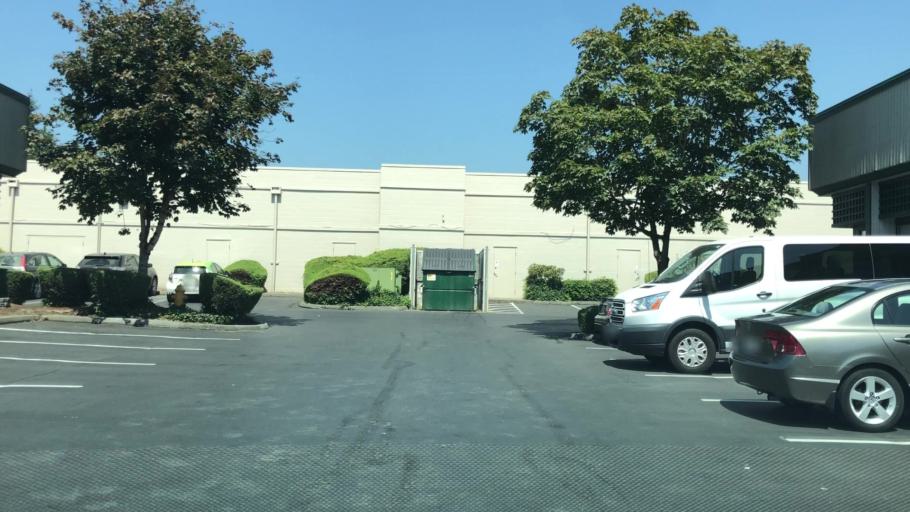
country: US
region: Washington
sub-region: King County
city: Woodinville
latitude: 47.7528
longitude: -122.1607
